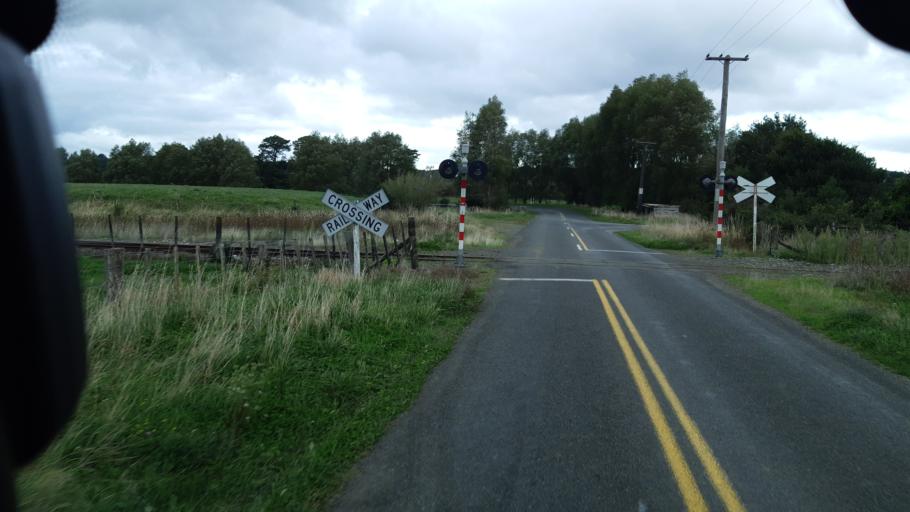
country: NZ
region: Manawatu-Wanganui
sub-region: Palmerston North City
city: Palmerston North
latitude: -40.5685
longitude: 175.6923
